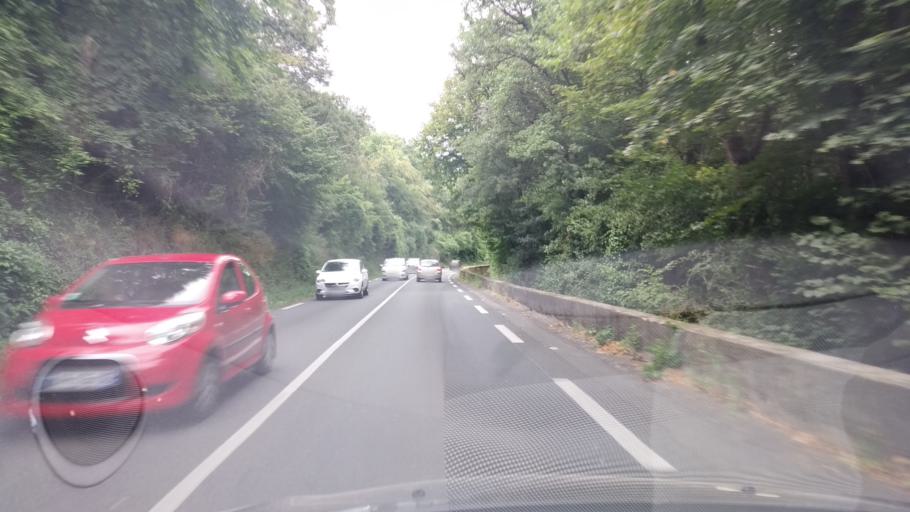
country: FR
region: Poitou-Charentes
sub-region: Departement de la Vienne
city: Saint-Benoit
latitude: 46.5487
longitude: 0.3511
